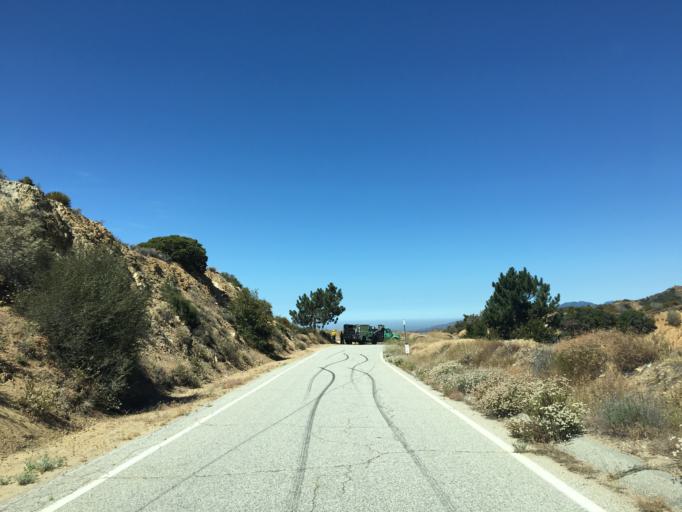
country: US
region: California
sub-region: San Bernardino County
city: San Antonio Heights
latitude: 34.2193
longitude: -117.7115
